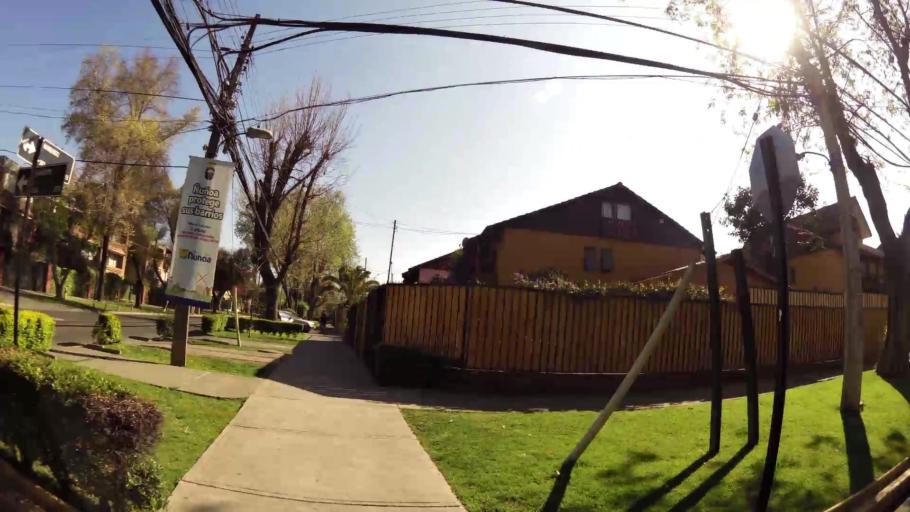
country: CL
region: Santiago Metropolitan
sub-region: Provincia de Santiago
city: Villa Presidente Frei, Nunoa, Santiago, Chile
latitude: -33.4516
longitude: -70.5763
